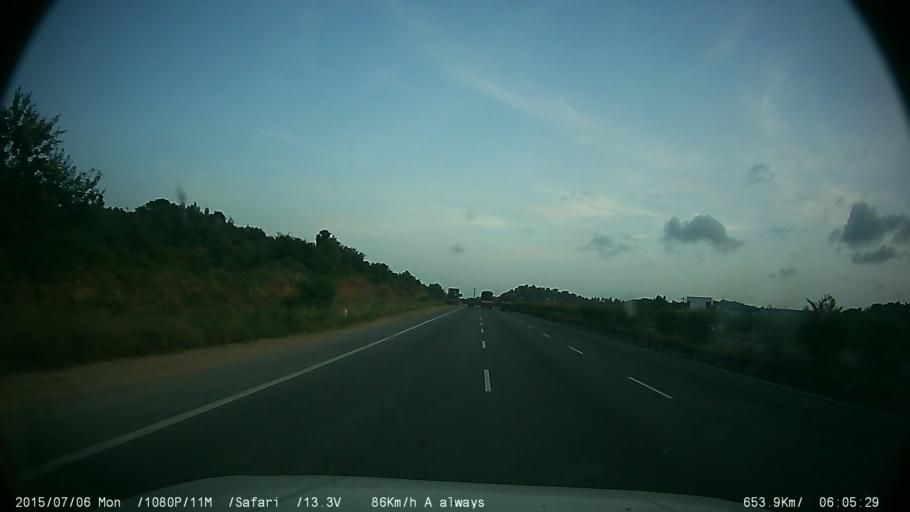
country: IN
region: Tamil Nadu
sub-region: Krishnagiri
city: Krishnagiri
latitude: 12.6242
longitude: 78.0803
